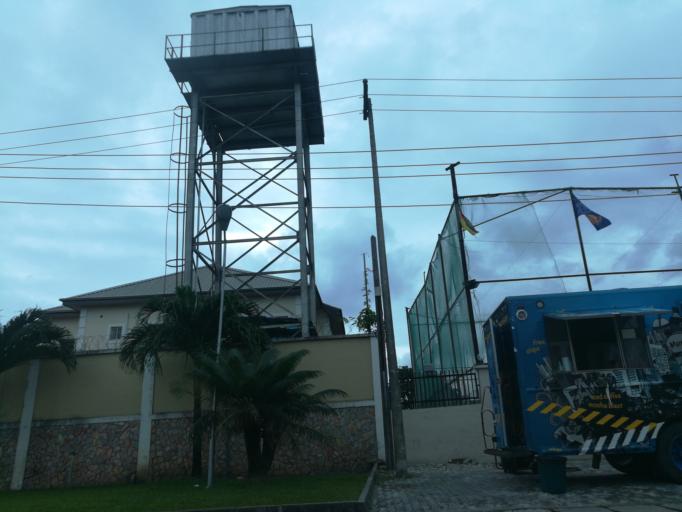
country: NG
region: Lagos
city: Ikoyi
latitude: 6.4458
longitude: 3.4641
